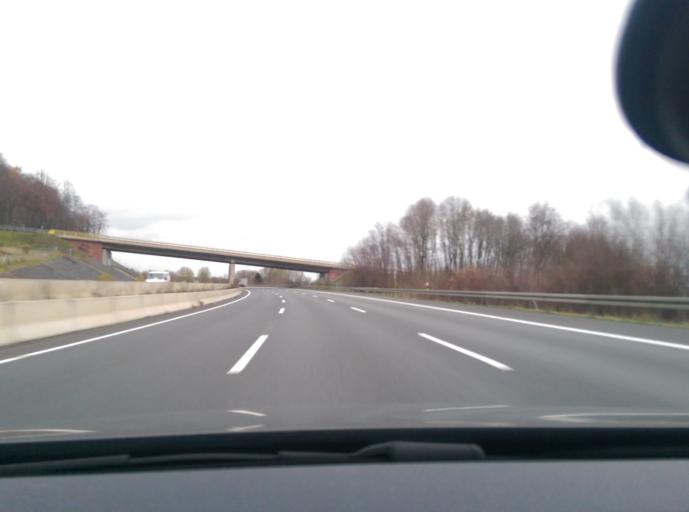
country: DE
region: Lower Saxony
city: Bovenden
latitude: 51.5821
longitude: 9.9126
